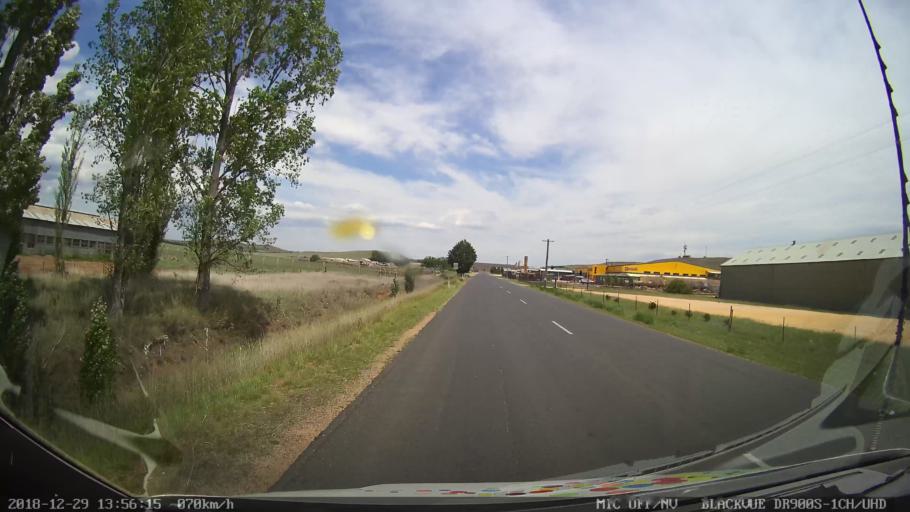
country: AU
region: New South Wales
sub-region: Cooma-Monaro
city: Cooma
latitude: -36.2287
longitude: 149.1465
